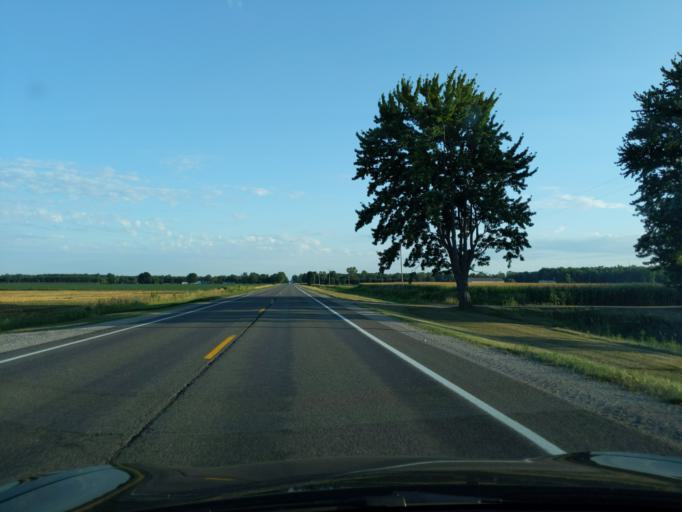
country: US
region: Michigan
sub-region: Gratiot County
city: Breckenridge
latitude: 43.4716
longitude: -84.3699
